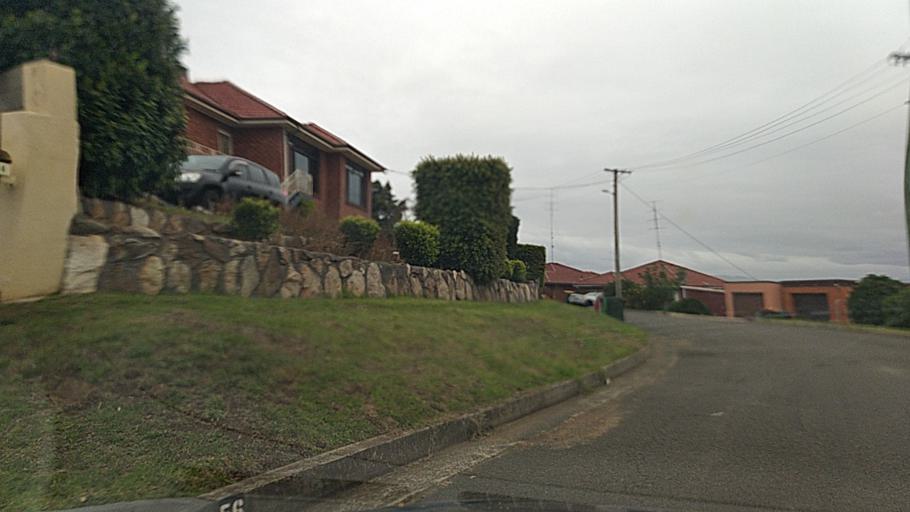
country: AU
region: New South Wales
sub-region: Wollongong
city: Lake Heights
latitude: -34.4878
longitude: 150.8779
